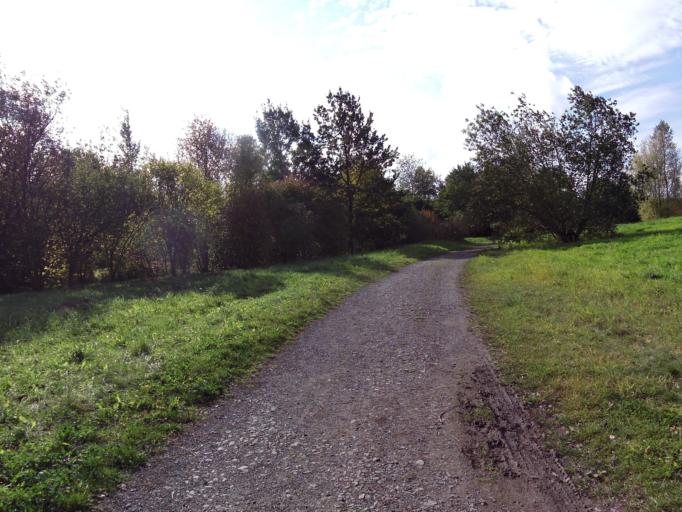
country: DE
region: Saxony
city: Grossposna
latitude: 51.3080
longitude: 12.4451
